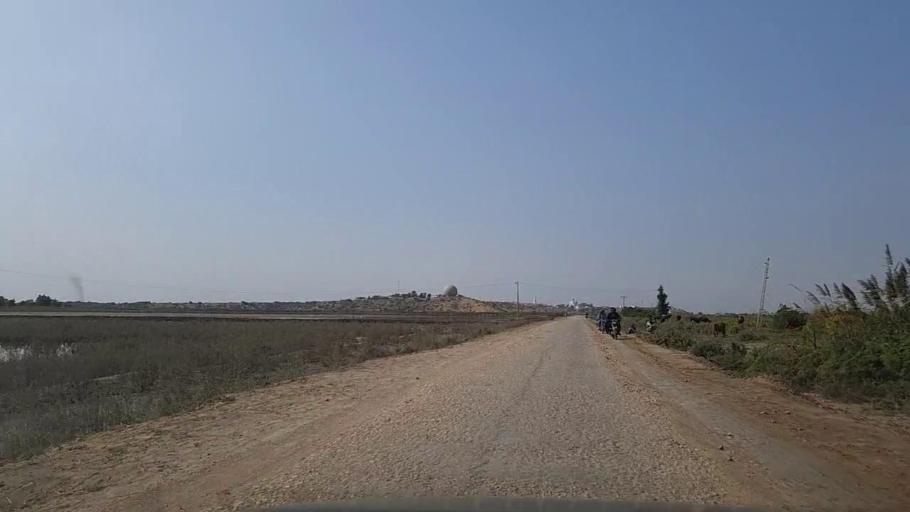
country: PK
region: Sindh
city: Chuhar Jamali
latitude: 24.5492
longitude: 67.8967
